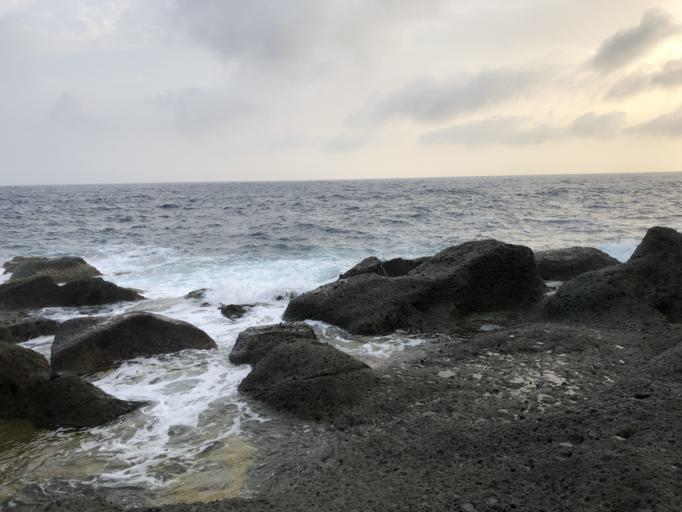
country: IT
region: Sardinia
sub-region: Provincia di Oristano
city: Bosa
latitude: 40.2993
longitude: 8.4663
